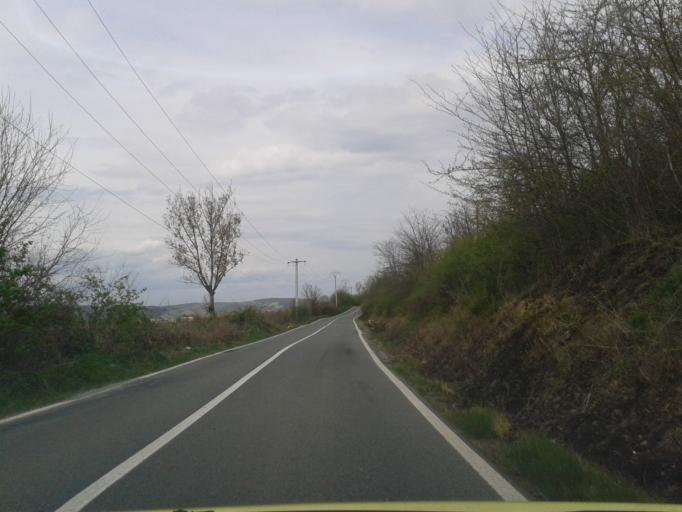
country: RO
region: Alba
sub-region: Municipiul Blaj
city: Veza
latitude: 46.1526
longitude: 23.9618
